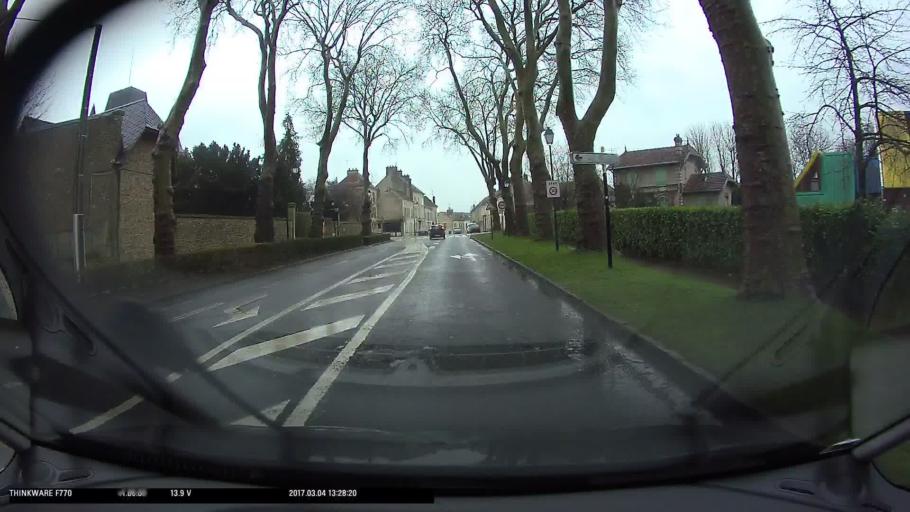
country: FR
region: Ile-de-France
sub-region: Departement du Val-d'Oise
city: Marines
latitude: 49.1464
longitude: 1.9758
